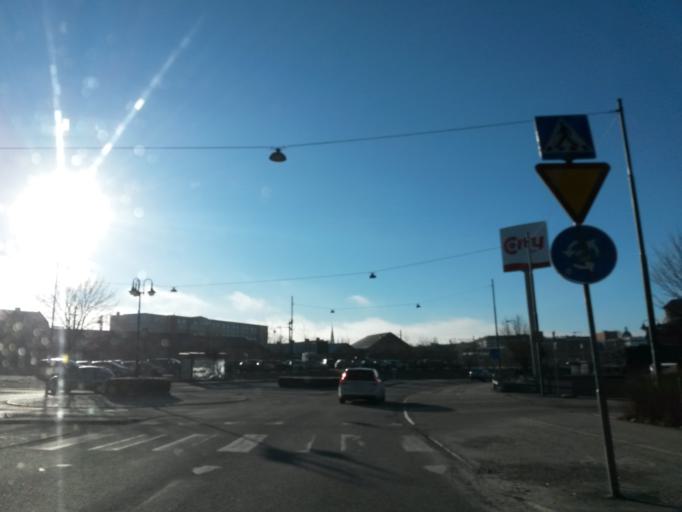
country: SE
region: Vaestra Goetaland
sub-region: Boras Kommun
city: Boras
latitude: 57.7302
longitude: 12.9401
